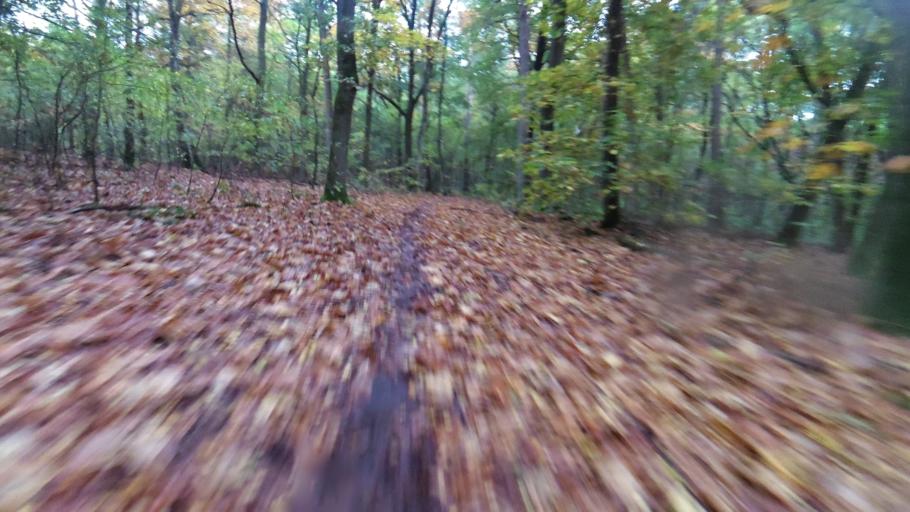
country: NL
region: Gelderland
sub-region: Gemeente Renkum
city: Wolfheze
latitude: 52.0020
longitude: 5.8159
